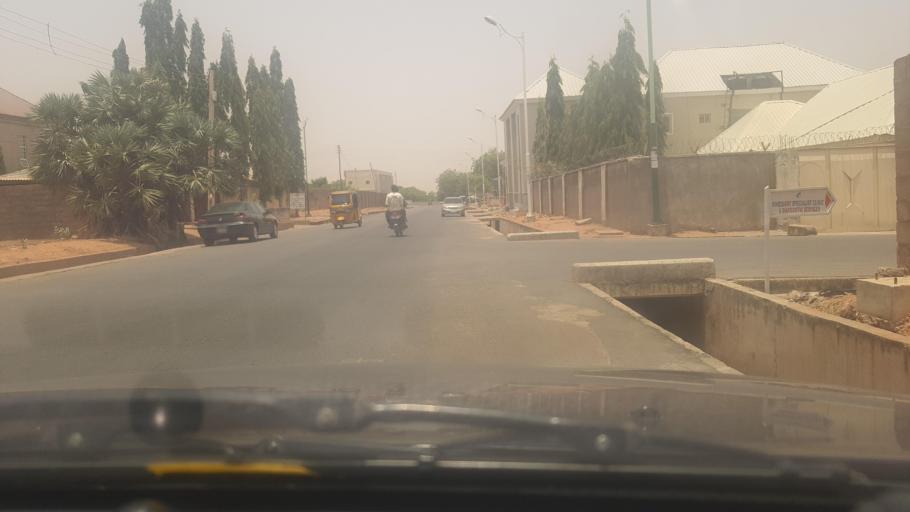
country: NG
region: Gombe
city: Gombe
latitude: 10.3059
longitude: 11.1485
